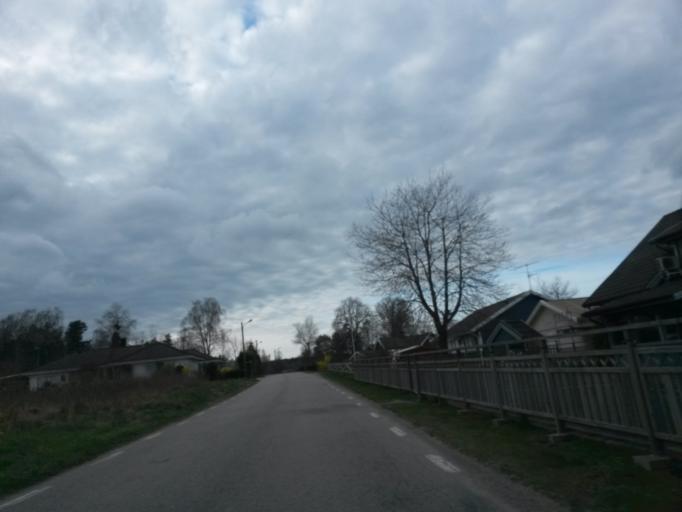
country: SE
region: Vaestra Goetaland
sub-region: Vargarda Kommun
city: Jonstorp
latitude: 58.0239
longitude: 12.6376
